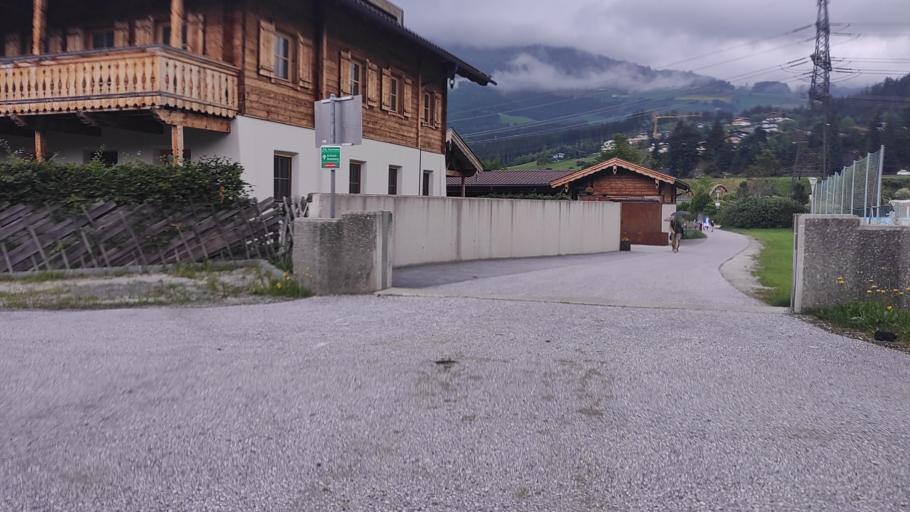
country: AT
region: Salzburg
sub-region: Politischer Bezirk Zell am See
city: Hollersbach im Pinzgau
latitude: 47.2764
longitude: 12.4173
